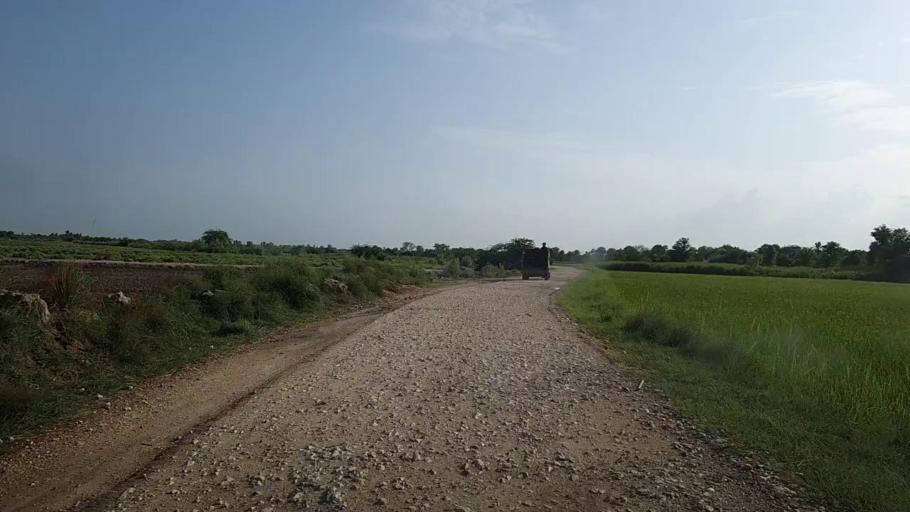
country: PK
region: Sindh
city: Pad Idan
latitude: 26.8258
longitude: 68.2386
